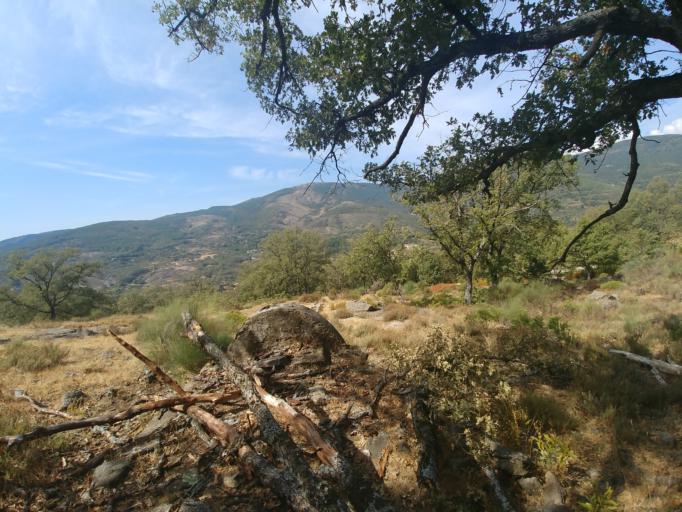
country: ES
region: Extremadura
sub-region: Provincia de Caceres
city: Garganta la Olla
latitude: 40.1070
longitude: -5.7648
